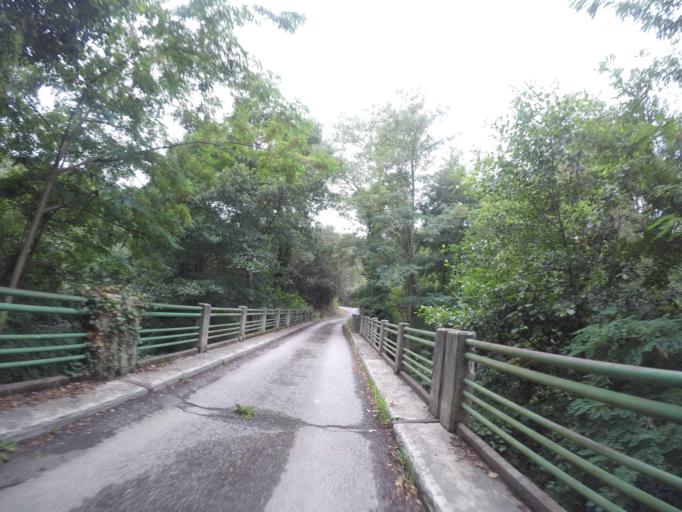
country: FR
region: Languedoc-Roussillon
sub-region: Departement des Pyrenees-Orientales
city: Ille-sur-Tet
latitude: 42.6089
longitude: 2.6076
